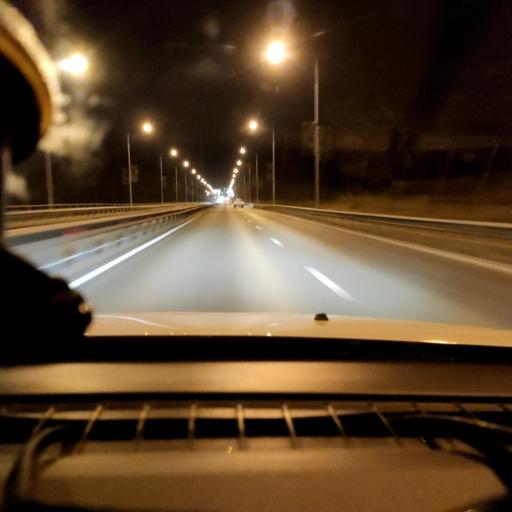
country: RU
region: Samara
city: Volzhskiy
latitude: 53.3619
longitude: 50.2034
